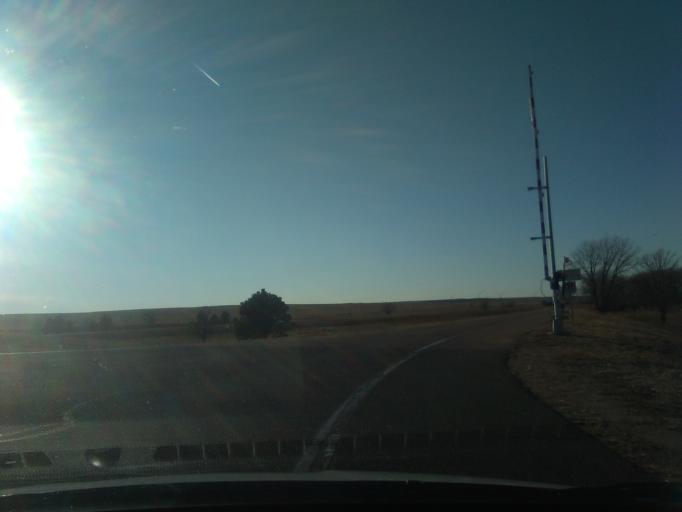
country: US
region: Nebraska
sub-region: Deuel County
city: Chappell
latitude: 41.0823
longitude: -102.4729
